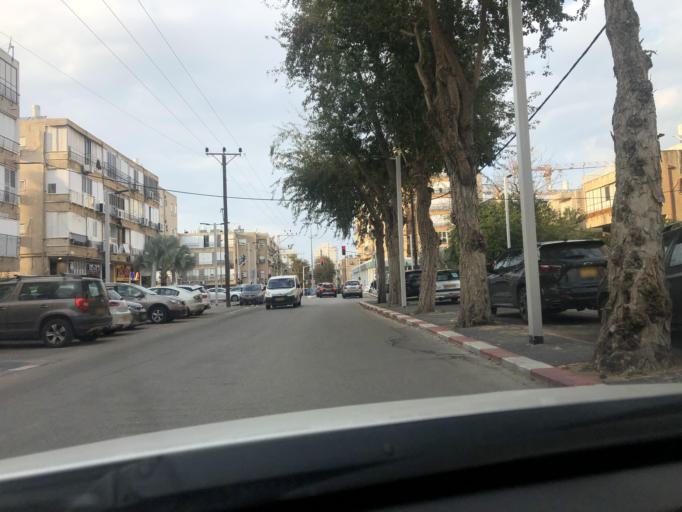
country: IL
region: Tel Aviv
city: Bat Yam
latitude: 32.0213
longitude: 34.7501
